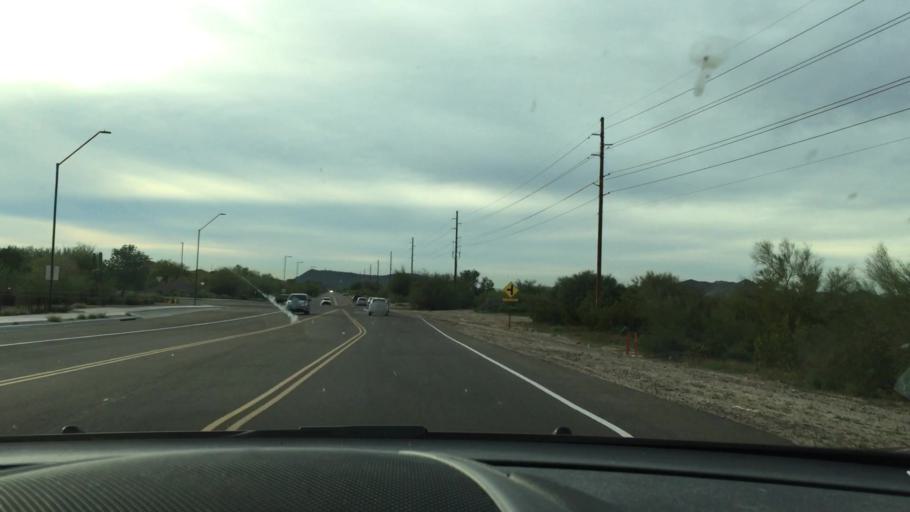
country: US
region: Arizona
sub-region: Maricopa County
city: Cave Creek
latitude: 33.6987
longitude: -111.9813
